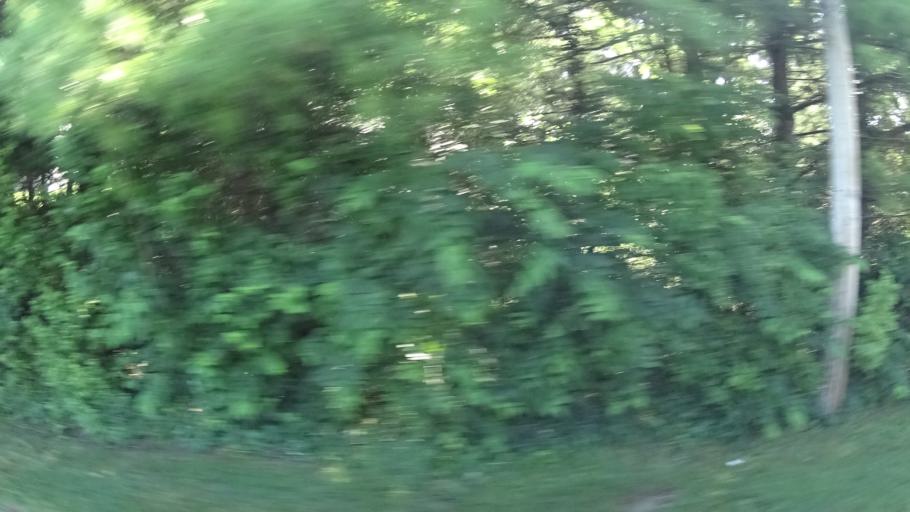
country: US
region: Indiana
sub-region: Madison County
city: Ingalls
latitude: 39.9756
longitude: -85.8150
